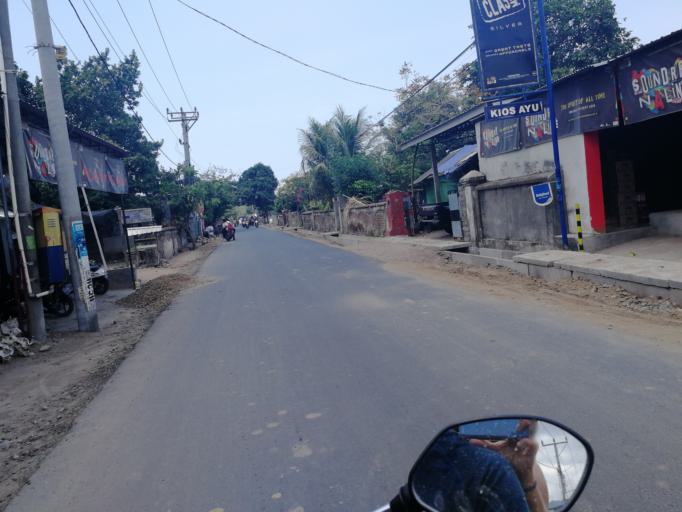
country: ID
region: West Nusa Tenggara
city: Pemenang
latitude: -8.4037
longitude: 116.1025
